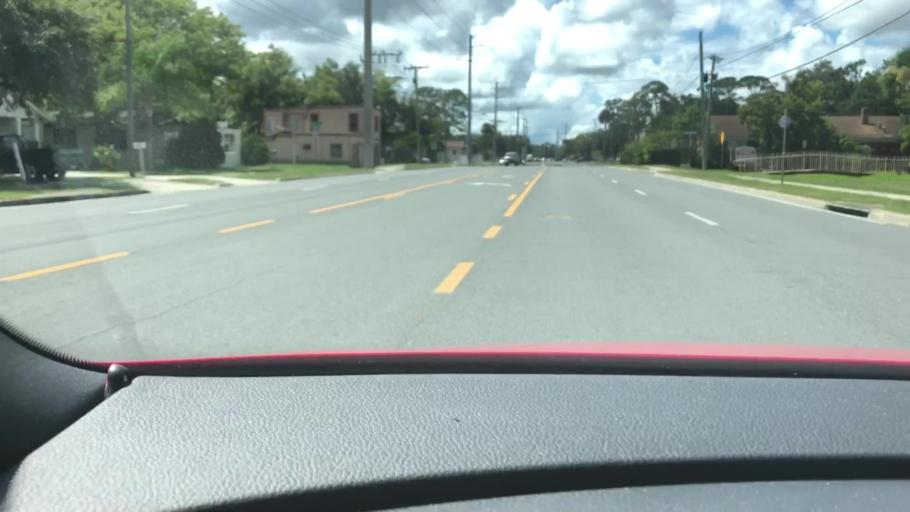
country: US
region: Florida
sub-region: Volusia County
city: Daytona Beach
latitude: 29.2132
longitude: -81.0365
